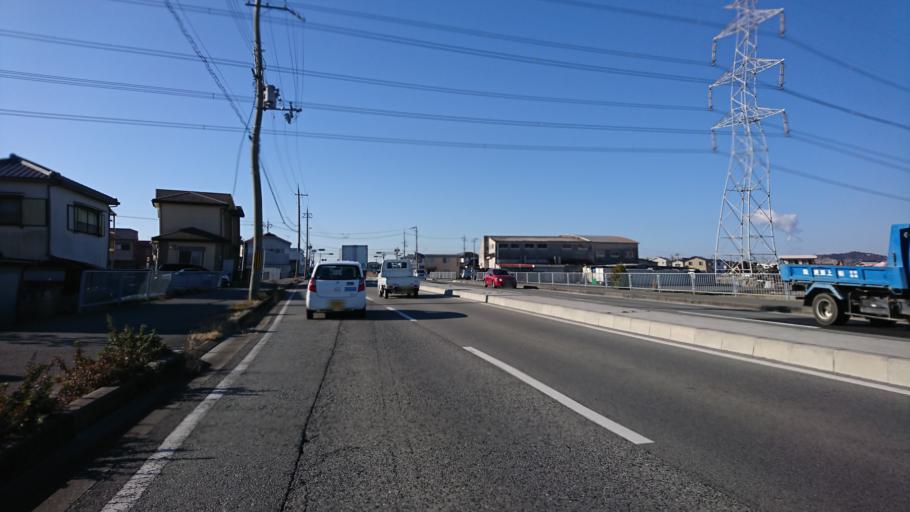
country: JP
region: Hyogo
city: Kakogawacho-honmachi
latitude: 34.7985
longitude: 134.8289
